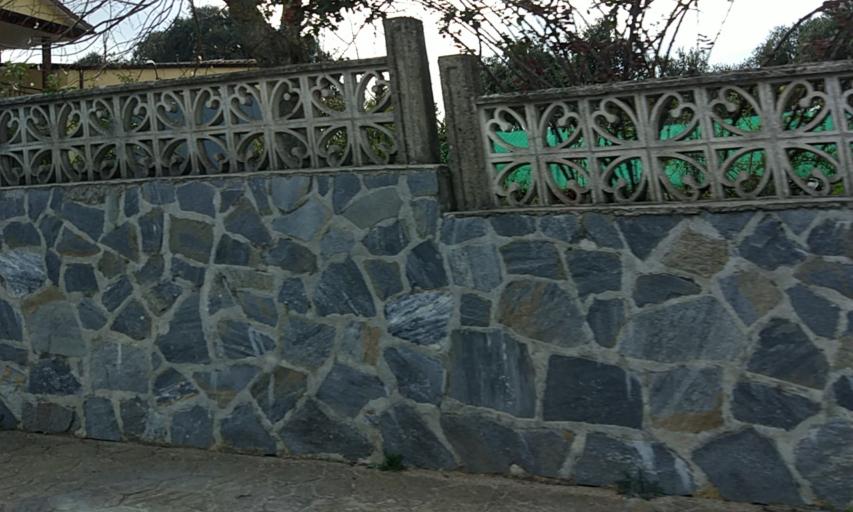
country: ES
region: Castille and Leon
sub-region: Provincia de Salamanca
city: Robleda
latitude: 40.3843
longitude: -6.6095
